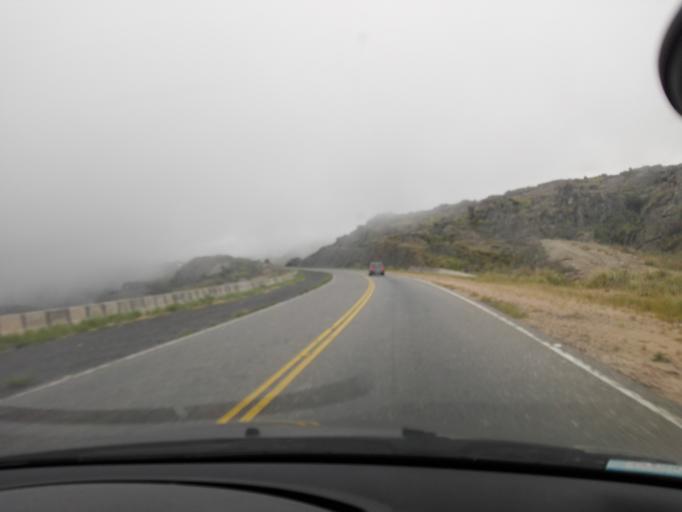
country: AR
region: Cordoba
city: Cuesta Blanca
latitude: -31.6094
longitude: -64.7381
